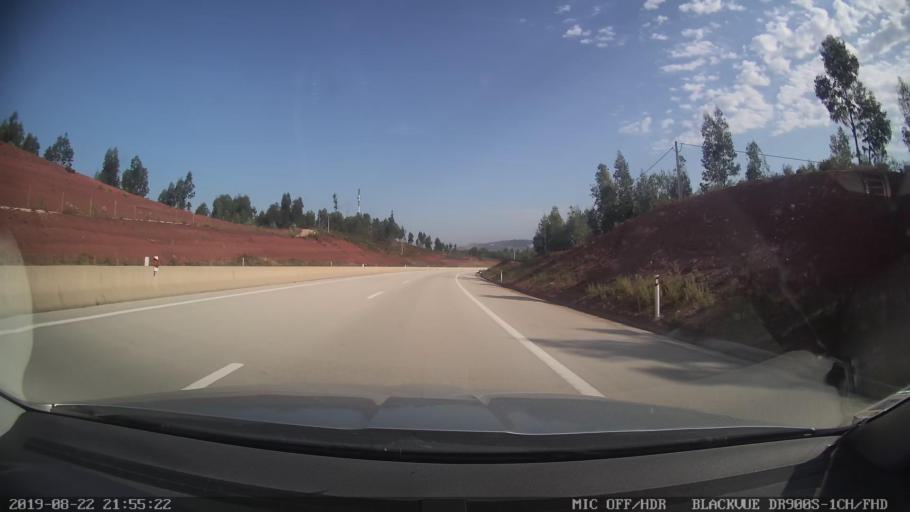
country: PT
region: Coimbra
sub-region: Coimbra
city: Coimbra
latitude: 40.1524
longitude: -8.3850
